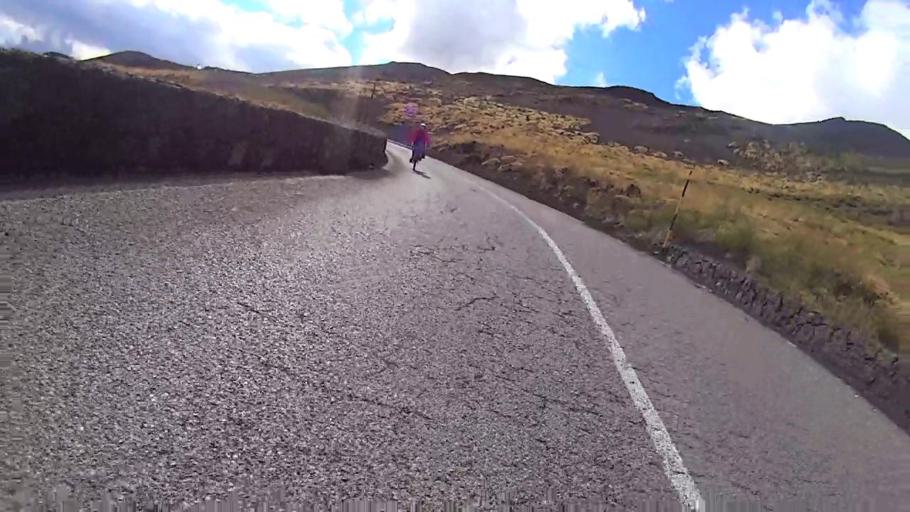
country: IT
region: Sicily
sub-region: Catania
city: Nicolosi
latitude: 37.7018
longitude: 15.0132
